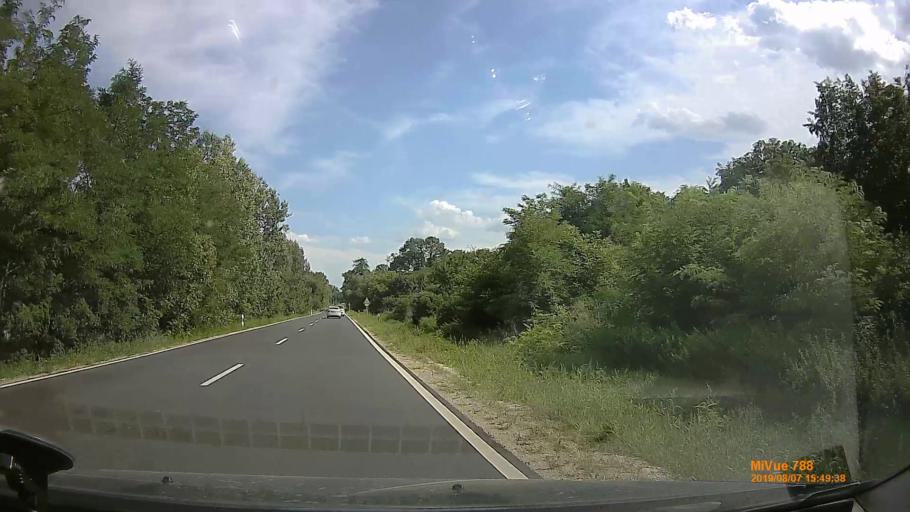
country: HU
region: Vas
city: Jak
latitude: 47.1481
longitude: 16.6434
